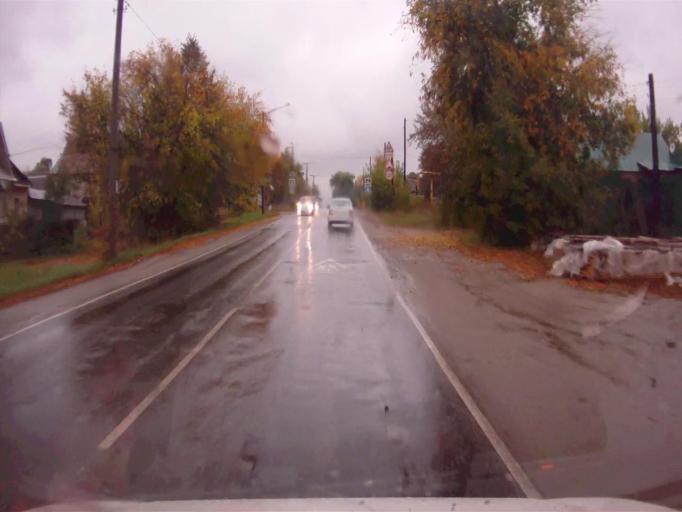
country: RU
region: Chelyabinsk
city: Kyshtym
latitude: 55.7218
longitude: 60.5338
